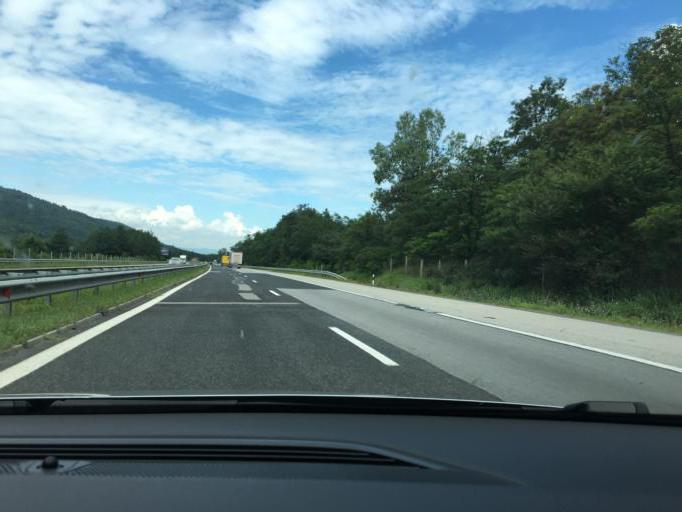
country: BG
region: Sofiya
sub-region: Obshtina Ikhtiman
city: Ikhtiman
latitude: 42.3688
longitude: 23.8899
